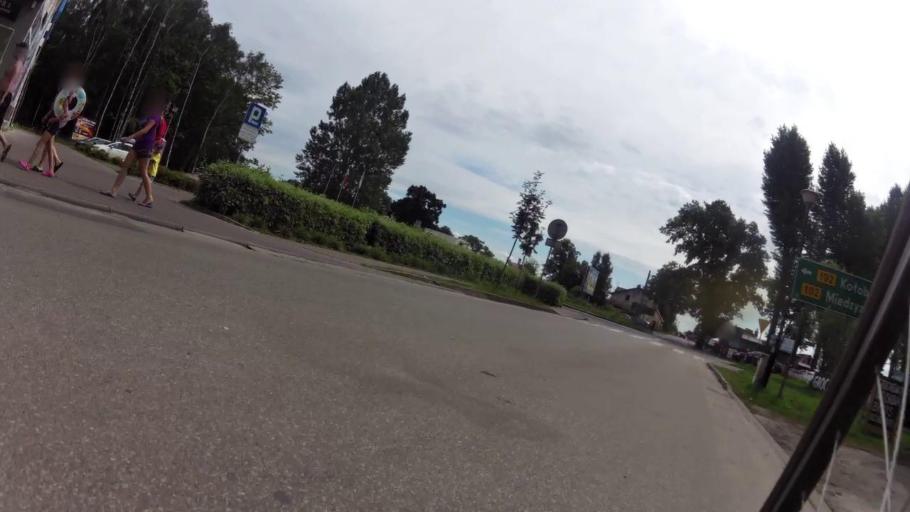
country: PL
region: West Pomeranian Voivodeship
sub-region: Powiat gryficki
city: Pobierowo
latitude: 54.0431
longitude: 14.8734
